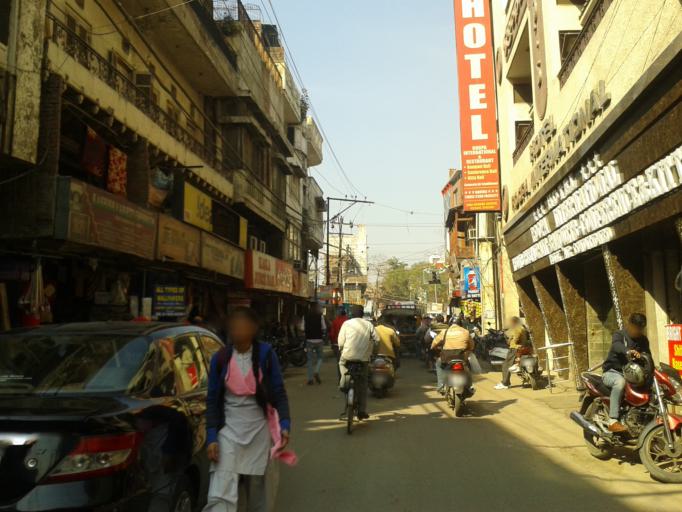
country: IN
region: Punjab
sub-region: Amritsar
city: Amritsar
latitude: 31.6301
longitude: 74.8734
